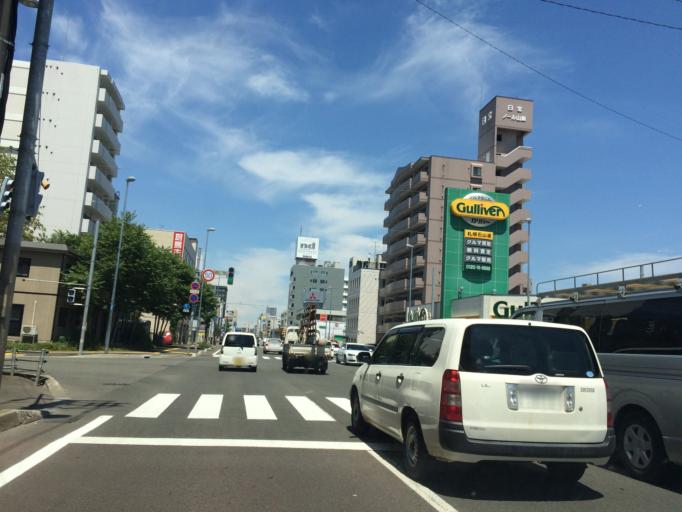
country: JP
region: Hokkaido
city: Sapporo
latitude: 43.0448
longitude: 141.3430
